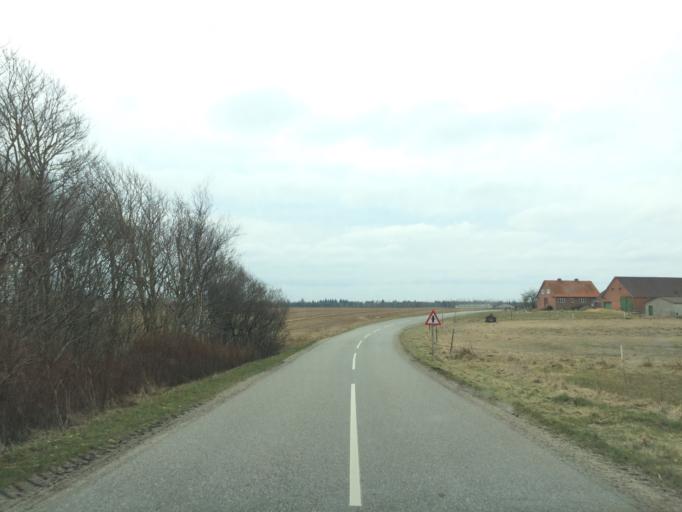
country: DK
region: Central Jutland
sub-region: Ringkobing-Skjern Kommune
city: Tarm
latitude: 55.8124
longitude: 8.3941
